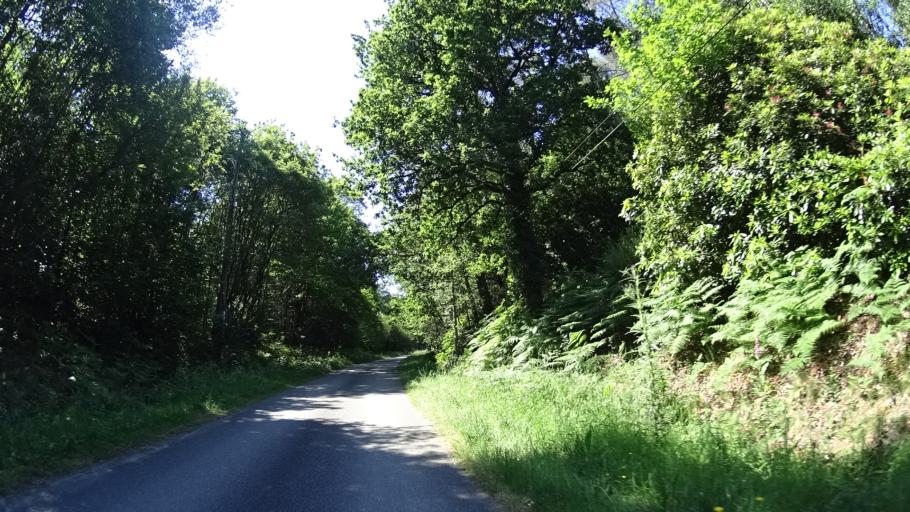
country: FR
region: Brittany
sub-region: Departement d'Ille-et-Vilaine
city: Langon
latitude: 47.7636
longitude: -1.8344
